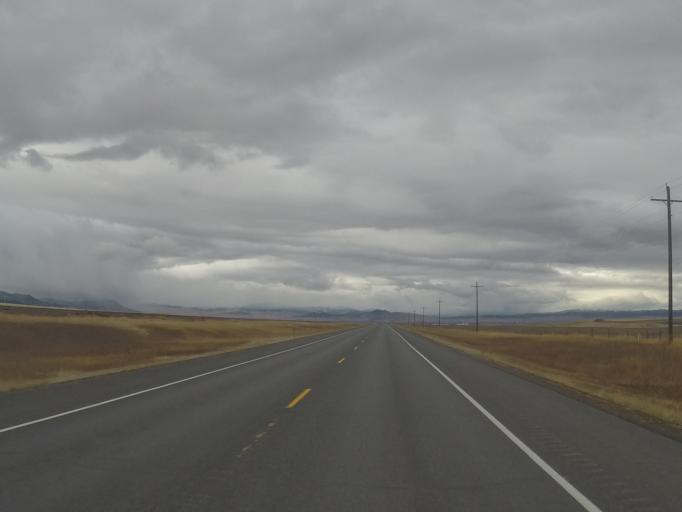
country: US
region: Montana
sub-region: Lewis and Clark County
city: East Helena
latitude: 46.5746
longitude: -111.8322
